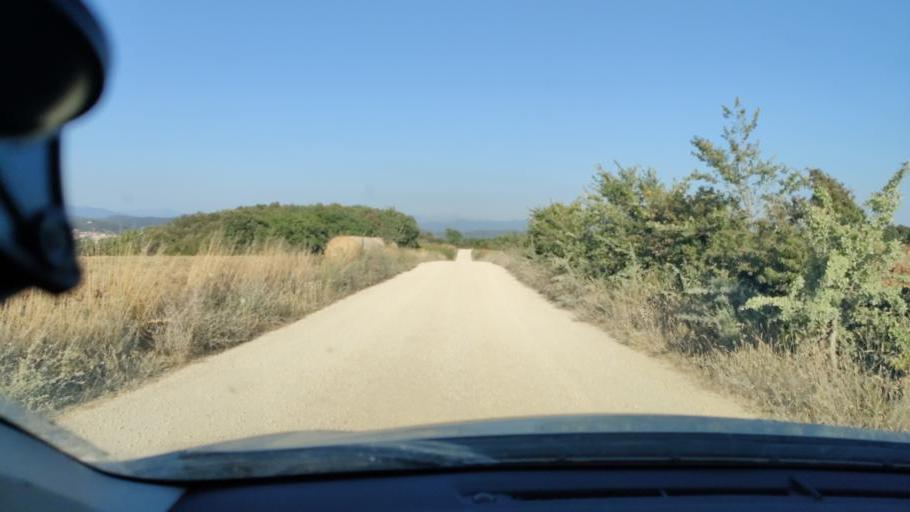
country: IT
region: Umbria
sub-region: Provincia di Terni
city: Penna in Teverina
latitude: 42.5392
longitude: 12.3733
